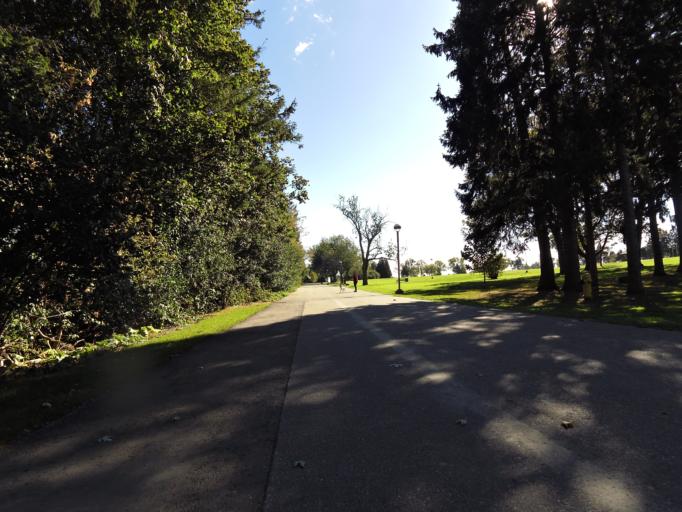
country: CA
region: Ontario
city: Ajax
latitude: 43.8508
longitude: -78.9404
